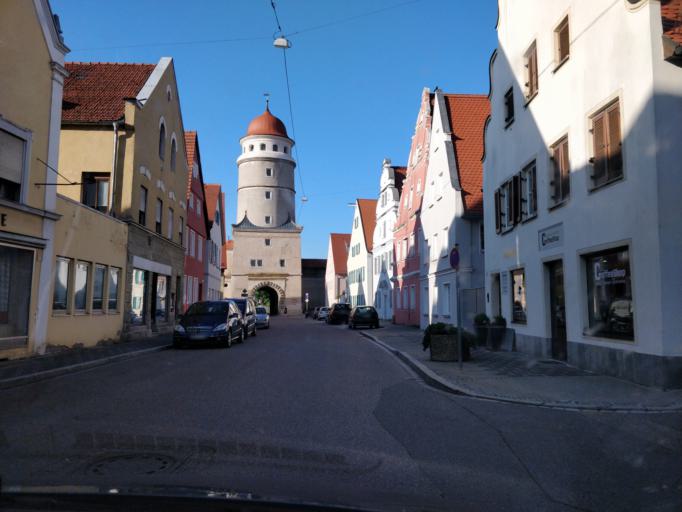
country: DE
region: Bavaria
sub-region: Swabia
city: Noerdlingen
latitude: 48.8535
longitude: 10.4920
